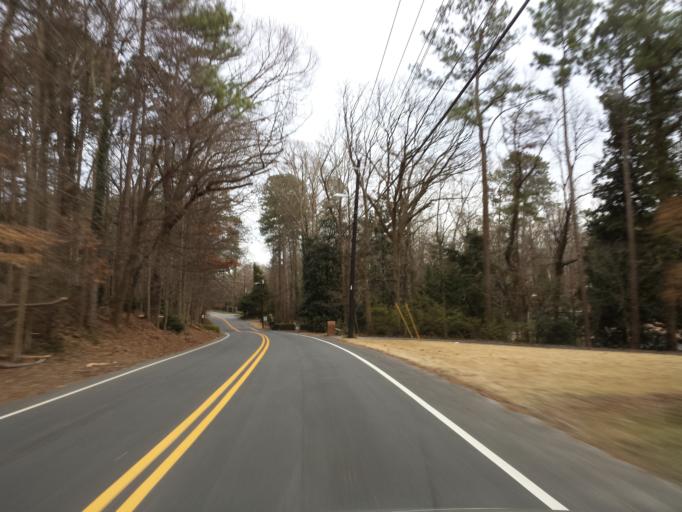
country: US
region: Georgia
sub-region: Cobb County
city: Vinings
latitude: 33.8792
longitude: -84.4145
